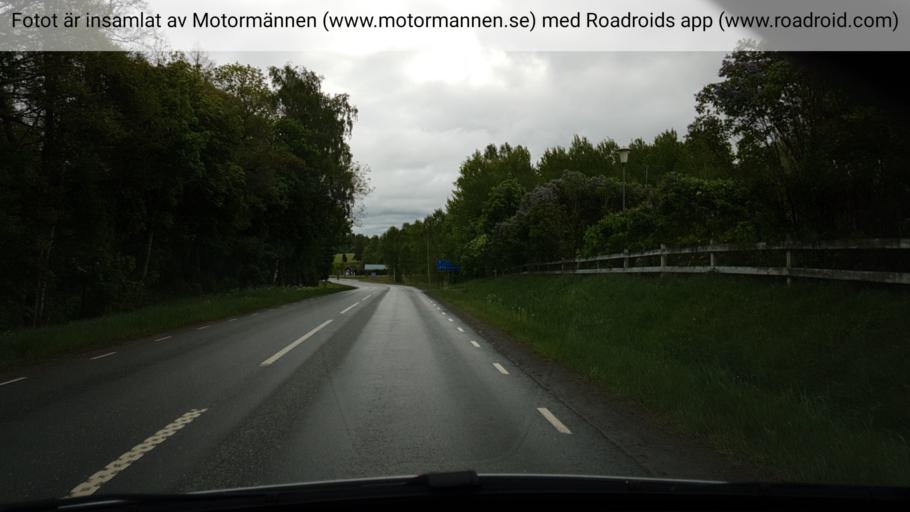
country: SE
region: Joenkoeping
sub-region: Aneby Kommun
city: Aneby
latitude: 57.8360
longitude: 14.7833
